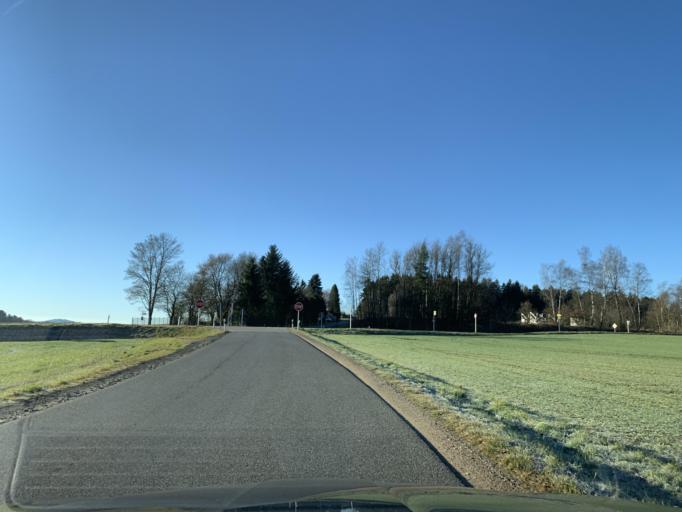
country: DE
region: Bavaria
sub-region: Upper Palatinate
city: Oberviechtach
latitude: 49.4518
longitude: 12.4413
